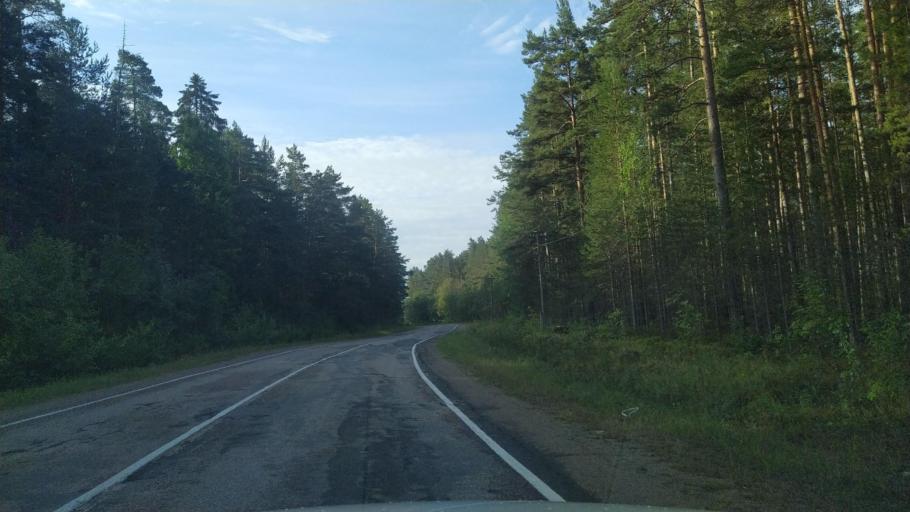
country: RU
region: Leningrad
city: Priozersk
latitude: 60.9702
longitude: 30.2843
